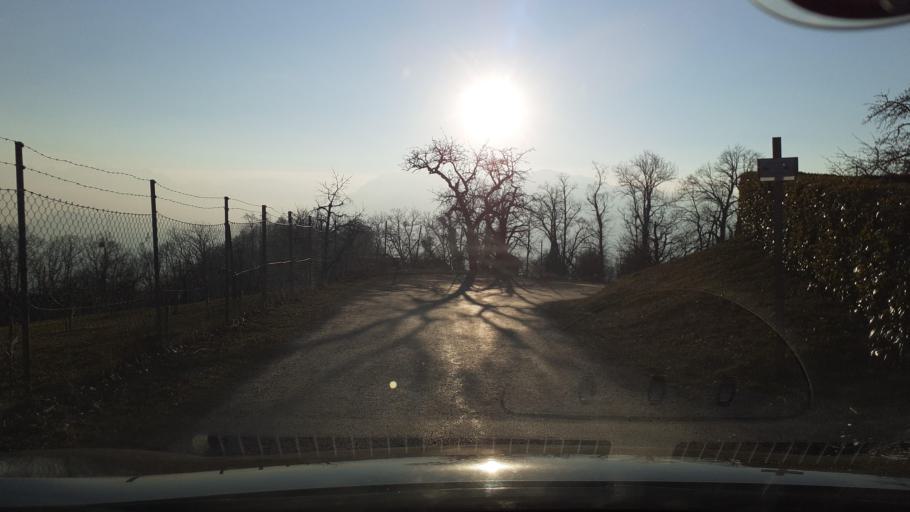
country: AT
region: Vorarlberg
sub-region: Politischer Bezirk Feldkirch
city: Fraxern
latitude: 47.3154
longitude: 9.6681
